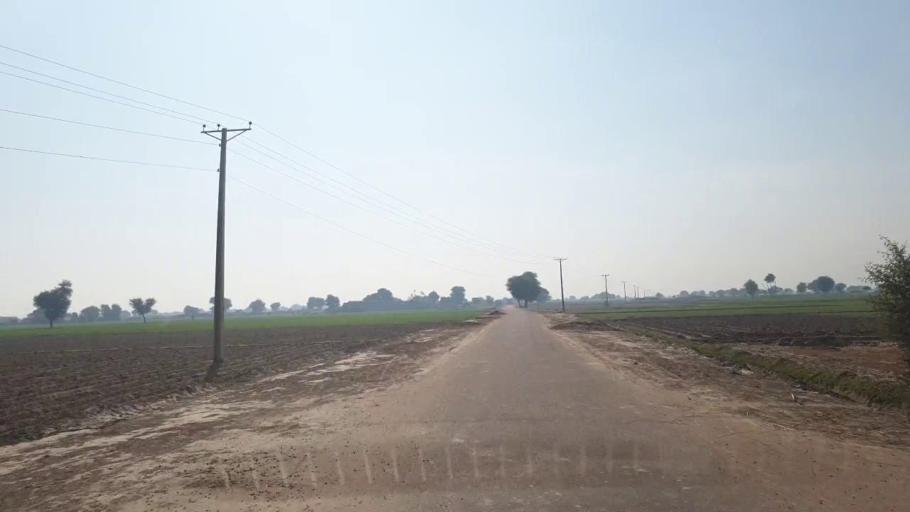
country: PK
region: Sindh
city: Shahpur Chakar
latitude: 26.1053
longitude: 68.6006
